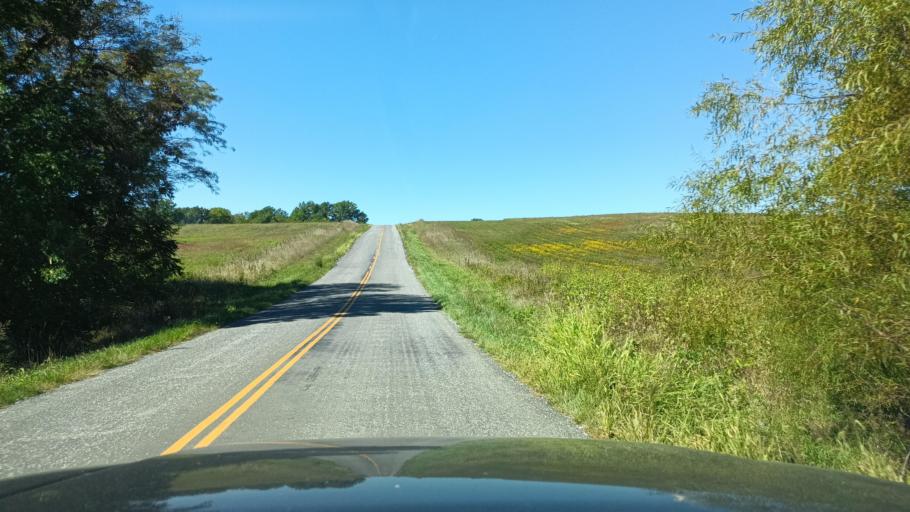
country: US
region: Missouri
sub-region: Adair County
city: Kirksville
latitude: 40.3302
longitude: -92.5350
